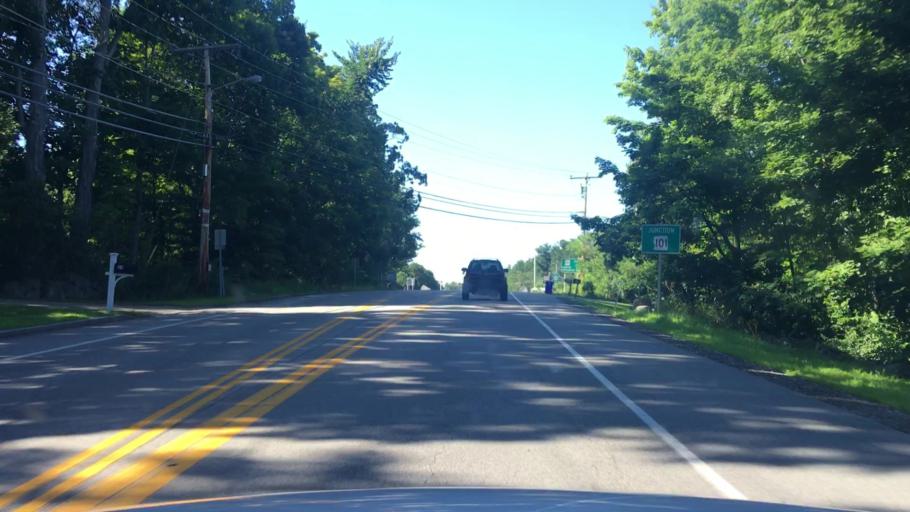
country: US
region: New Hampshire
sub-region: Rockingham County
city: Exeter
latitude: 42.9994
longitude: -70.9469
